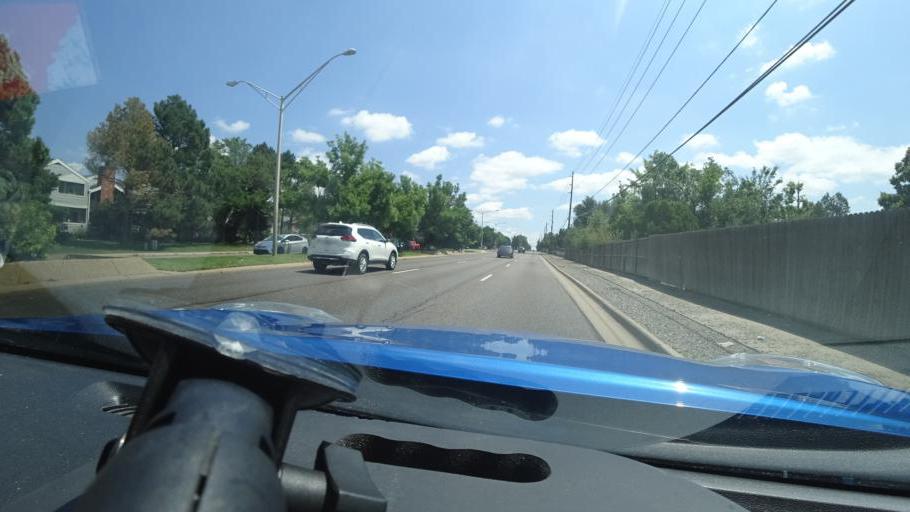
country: US
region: Colorado
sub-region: Adams County
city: Aurora
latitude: 39.7110
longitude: -104.8527
